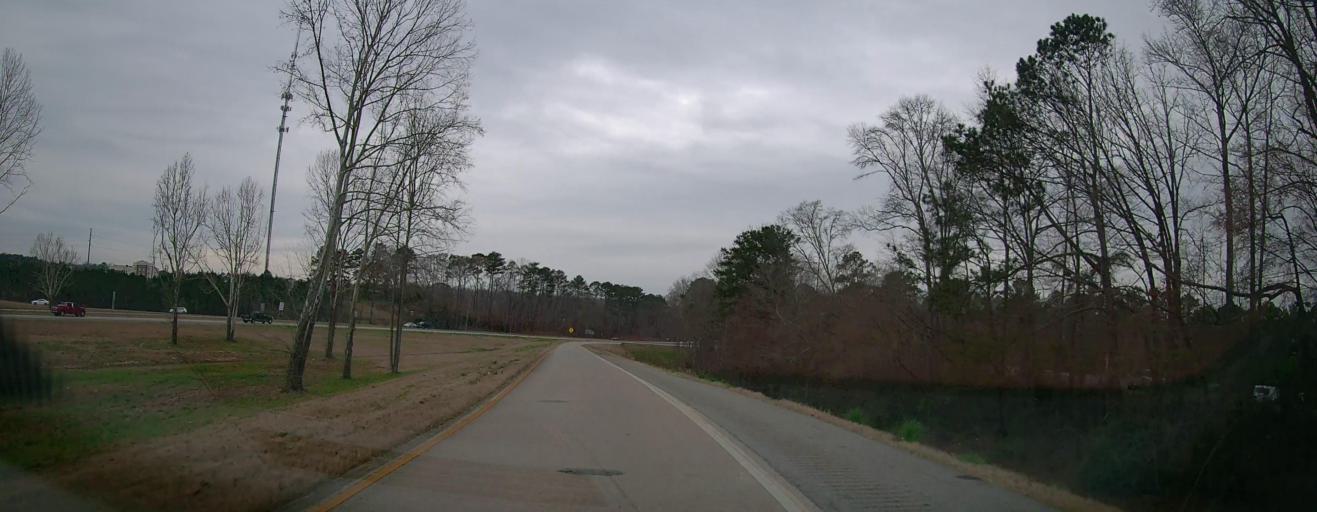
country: US
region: Georgia
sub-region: Bibb County
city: Macon
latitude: 32.9295
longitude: -83.7319
